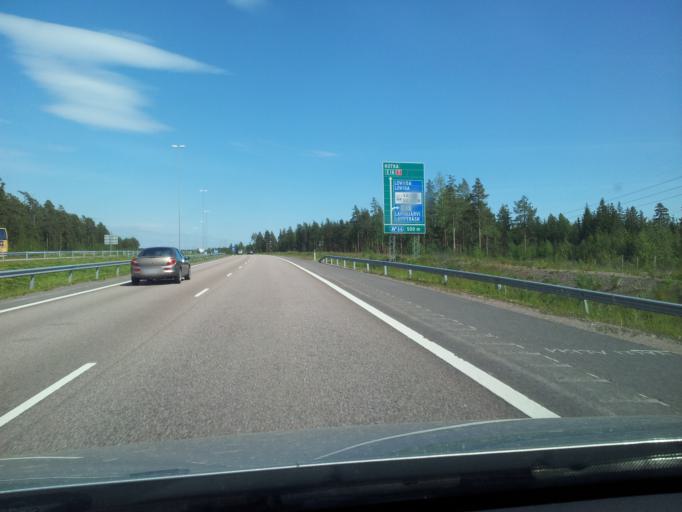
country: FI
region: Uusimaa
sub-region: Loviisa
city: Lovisa
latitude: 60.4587
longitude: 26.1735
